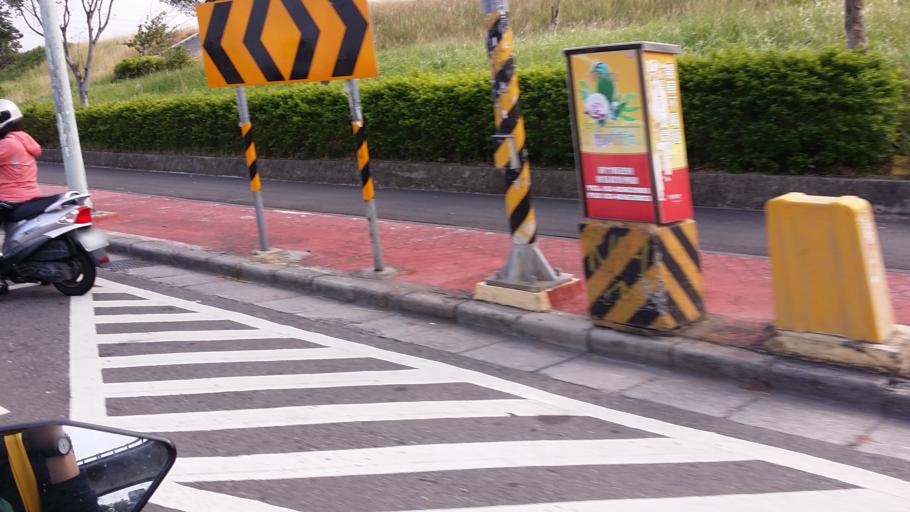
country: TW
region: Taiwan
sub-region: Hsinchu
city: Zhubei
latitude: 24.8243
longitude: 121.0002
